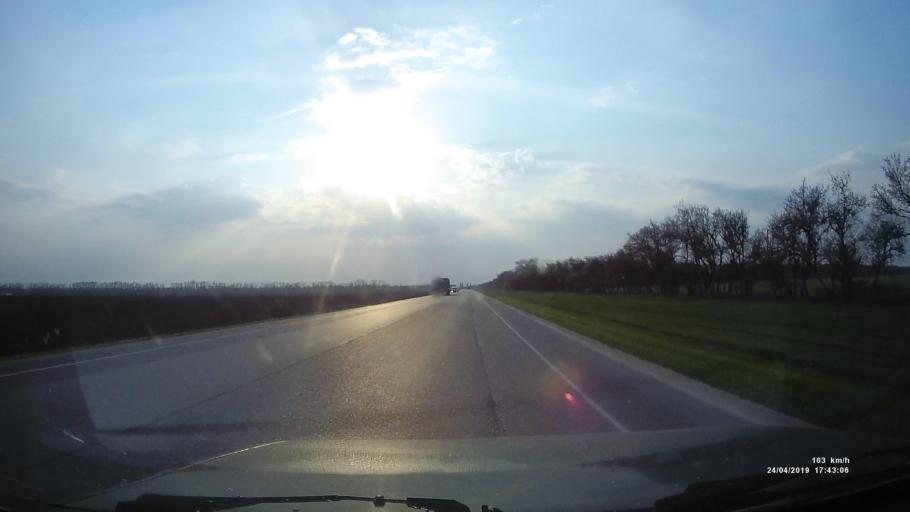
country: RU
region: Rostov
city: Tselina
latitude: 46.5327
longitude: 40.9340
